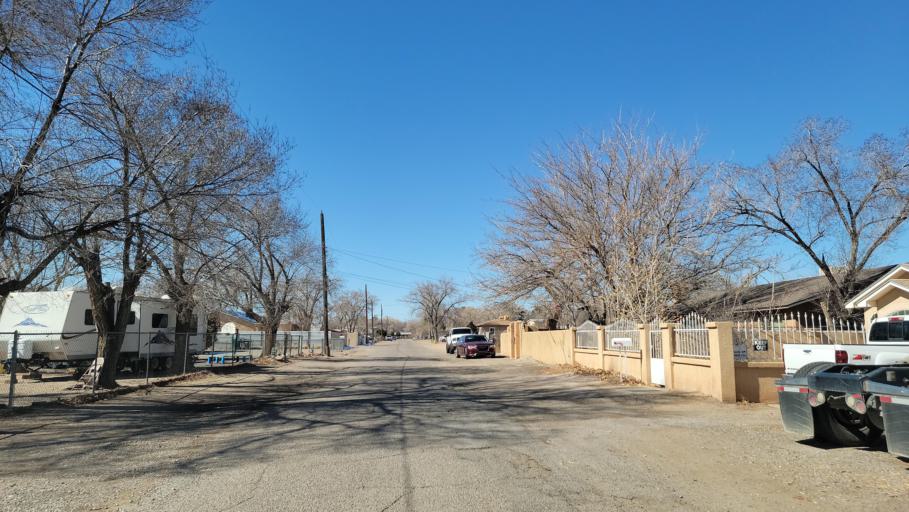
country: US
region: New Mexico
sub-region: Bernalillo County
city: South Valley
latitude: 35.0323
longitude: -106.6817
